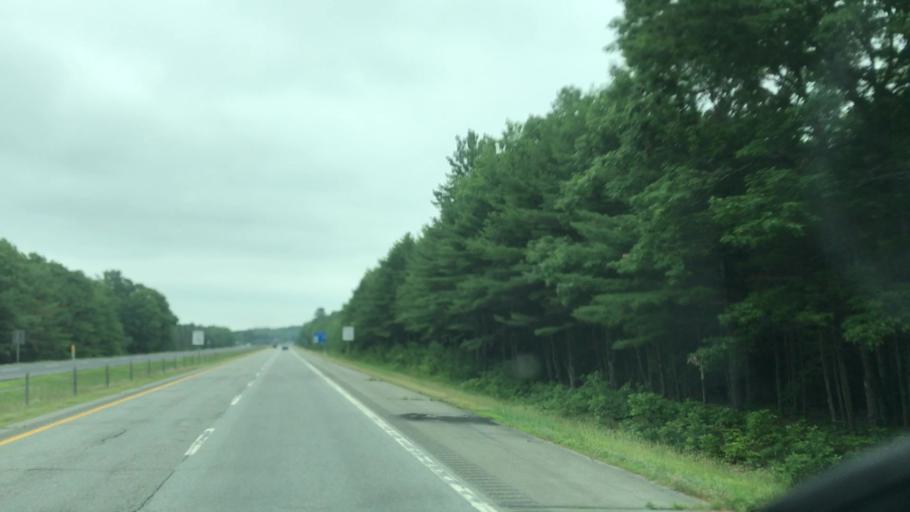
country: US
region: Maine
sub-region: Penobscot County
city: Orono
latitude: 44.9126
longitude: -68.6972
